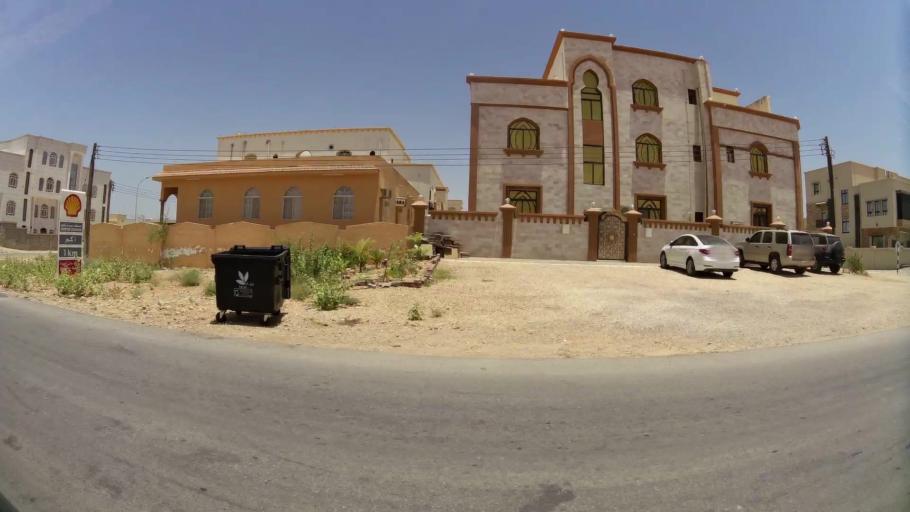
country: OM
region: Zufar
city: Salalah
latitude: 17.0914
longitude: 54.1601
